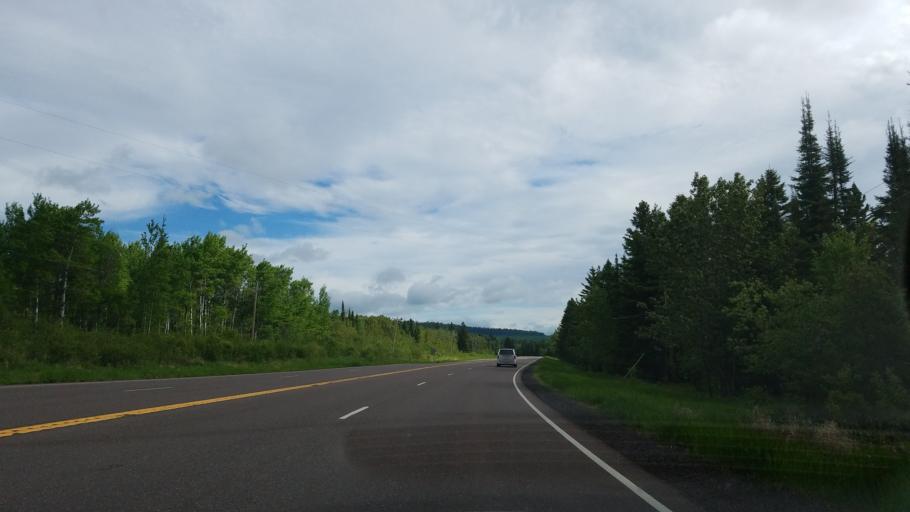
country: US
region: Minnesota
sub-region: Lake County
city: Two Harbors
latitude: 47.0802
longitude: -91.5849
